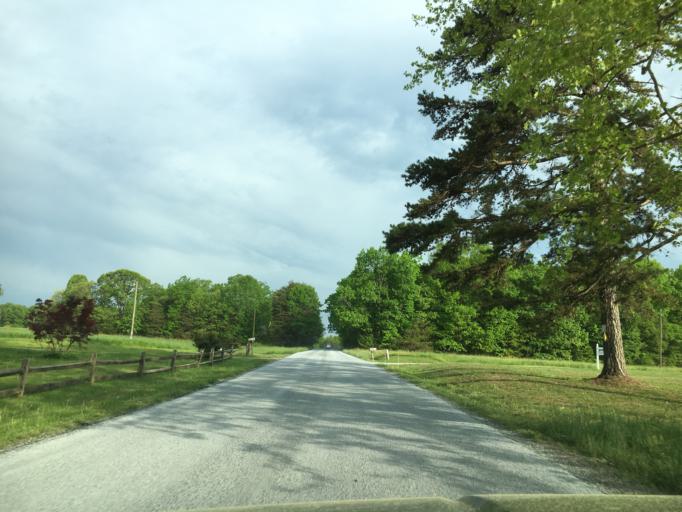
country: US
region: Virginia
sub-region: Campbell County
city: Brookneal
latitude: 36.9600
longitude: -78.9792
